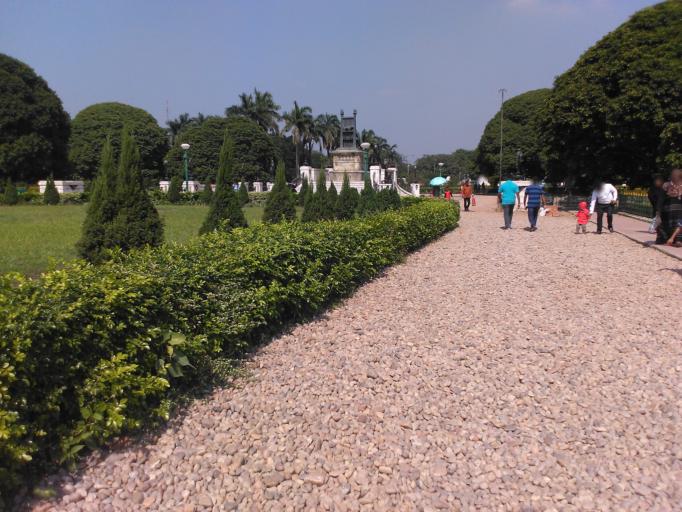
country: IN
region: West Bengal
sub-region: Kolkata
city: Bara Bazar
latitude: 22.5457
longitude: 88.3429
